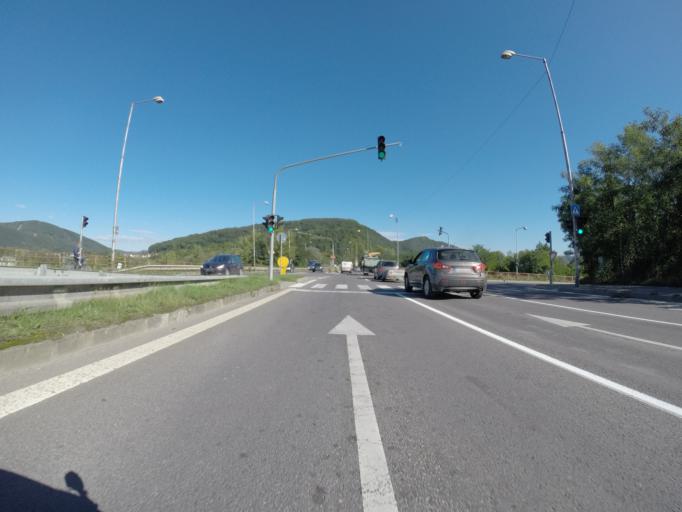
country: SK
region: Trenciansky
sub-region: Okres Povazska Bystrica
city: Povazska Bystrica
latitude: 49.1213
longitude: 18.4381
